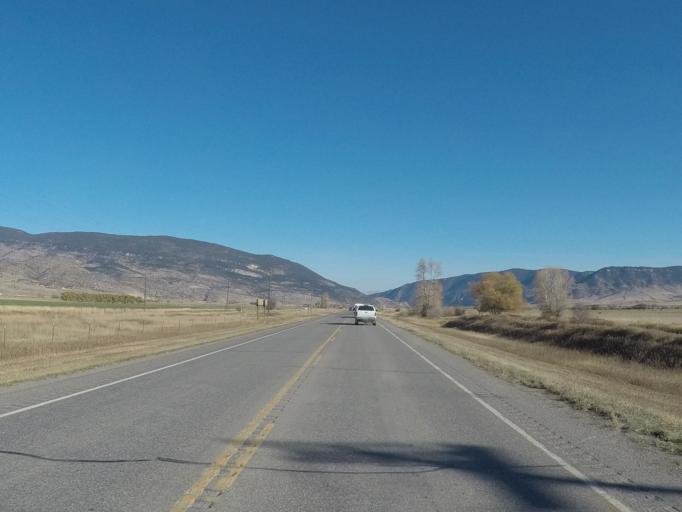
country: US
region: Montana
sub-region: Park County
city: Livingston
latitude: 45.5260
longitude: -110.6071
